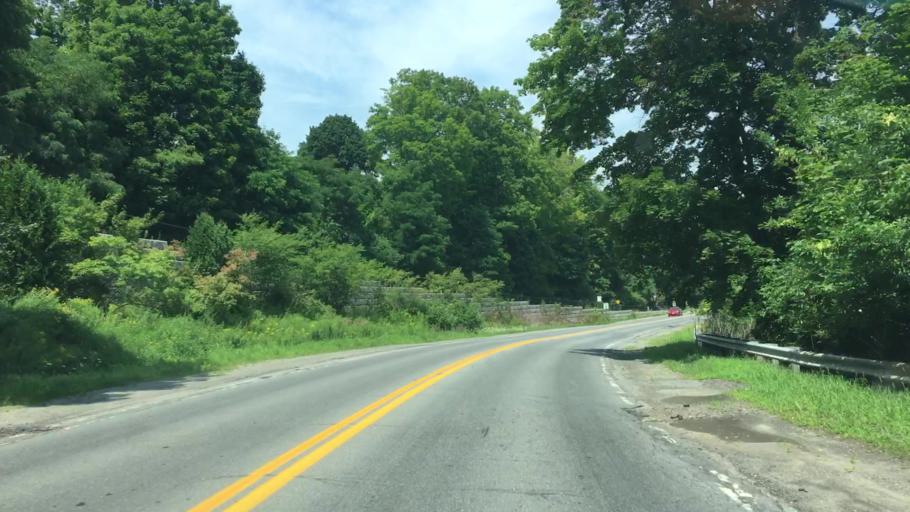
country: US
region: Maine
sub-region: Kennebec County
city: Hallowell
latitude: 44.2782
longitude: -69.7925
